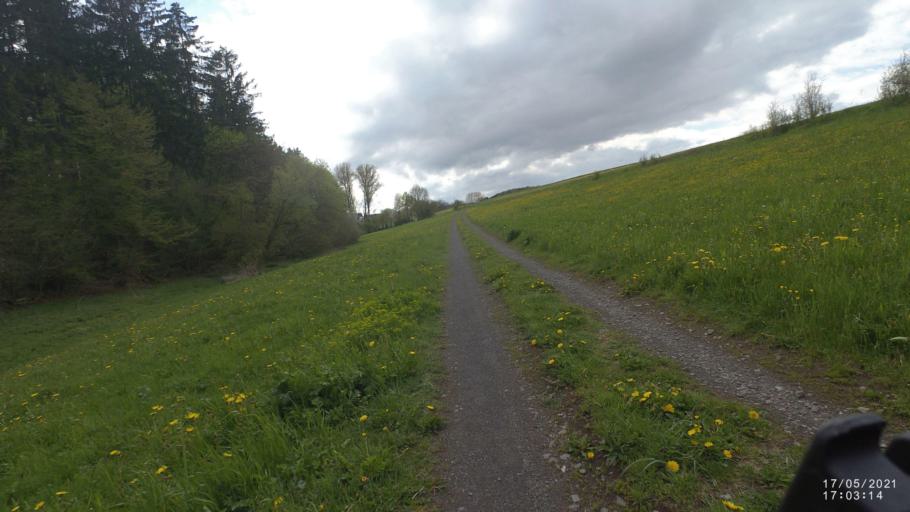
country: DE
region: Rheinland-Pfalz
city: Lind
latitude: 50.3137
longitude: 7.0291
